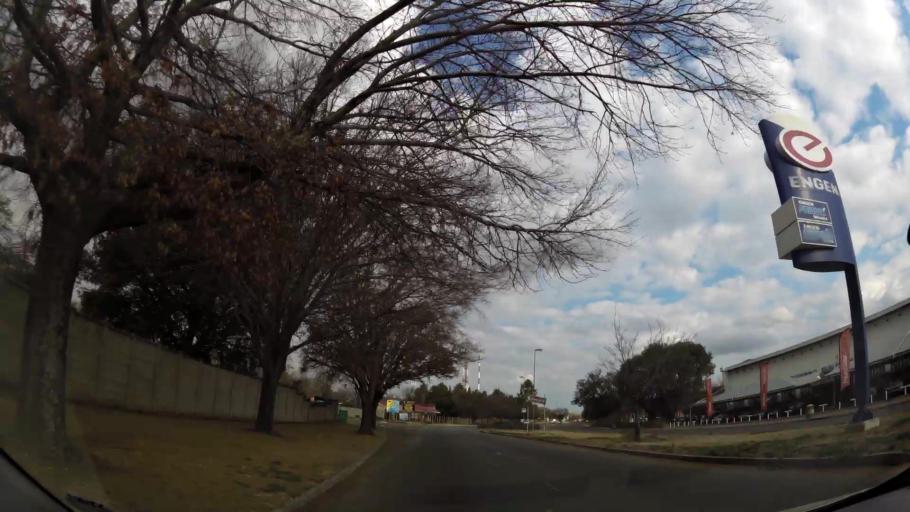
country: ZA
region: Orange Free State
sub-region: Fezile Dabi District Municipality
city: Sasolburg
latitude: -26.8139
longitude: 27.8296
